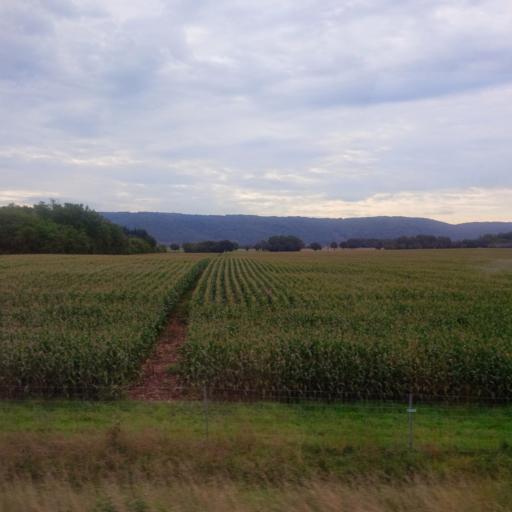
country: FR
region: Rhone-Alpes
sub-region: Departement de l'Ain
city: Certines
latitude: 46.1285
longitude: 5.2831
